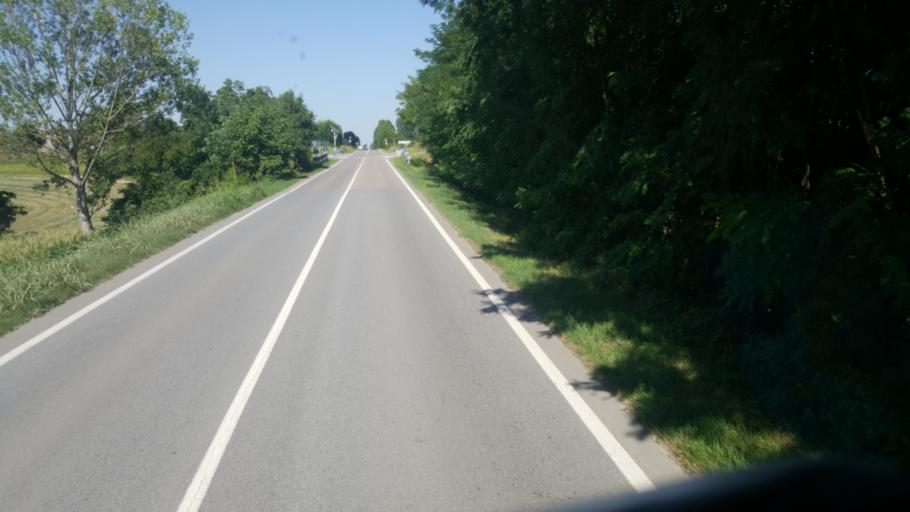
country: IT
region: Lombardy
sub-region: Provincia di Cremona
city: Isola Dovarese
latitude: 45.1921
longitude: 10.3286
